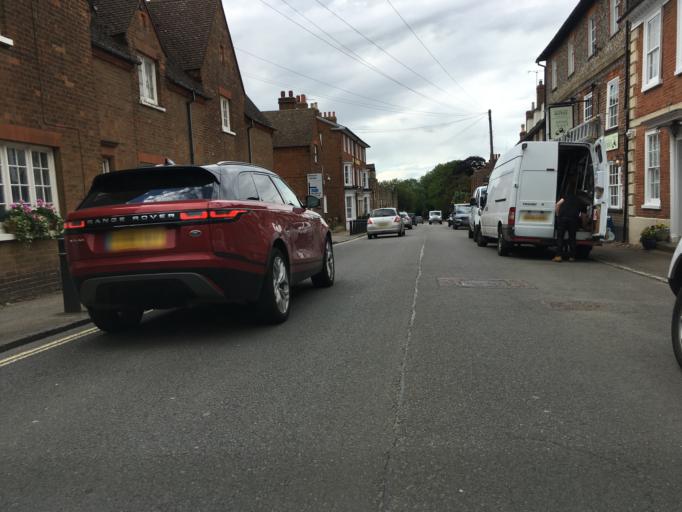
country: GB
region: England
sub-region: Central Bedfordshire
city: Woburn
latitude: 51.9901
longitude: -0.6197
